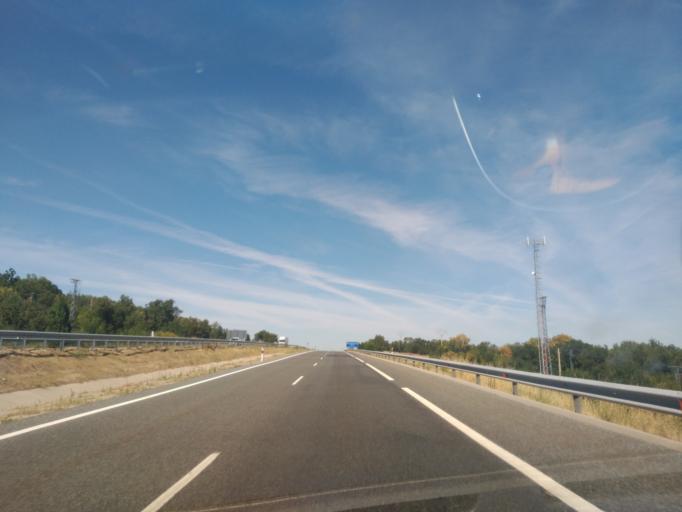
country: ES
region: Castille and Leon
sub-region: Provincia de Salamanca
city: Sorihuela
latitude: 40.4443
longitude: -5.6864
